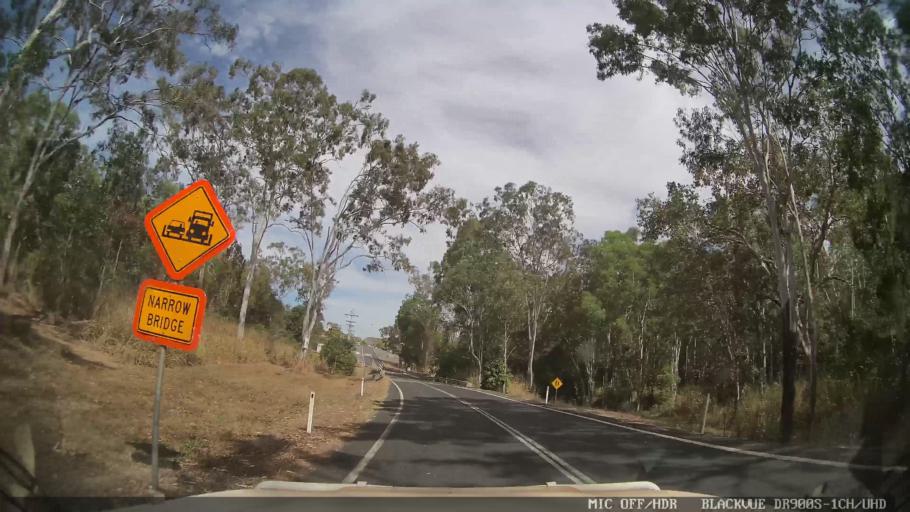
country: AU
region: Queensland
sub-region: Cairns
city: Port Douglas
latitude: -16.6709
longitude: 145.3288
